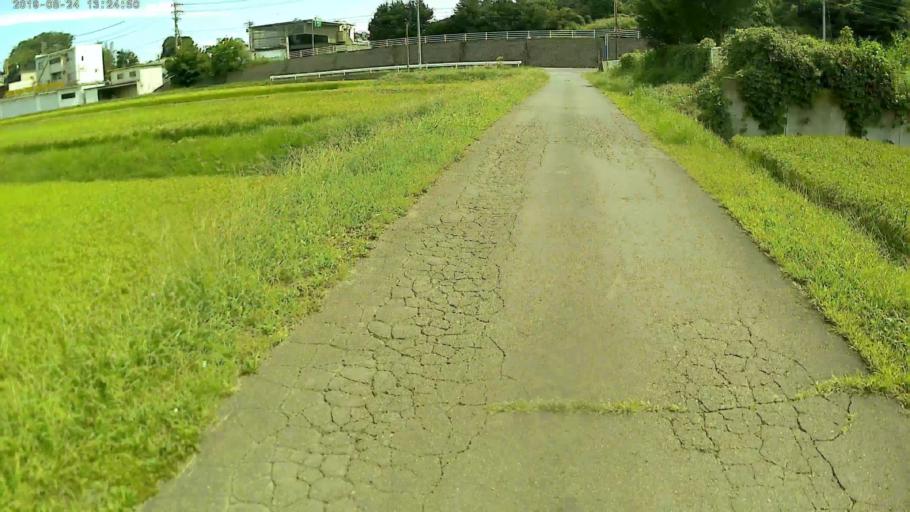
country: JP
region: Nagano
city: Komoro
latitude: 36.2707
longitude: 138.3857
